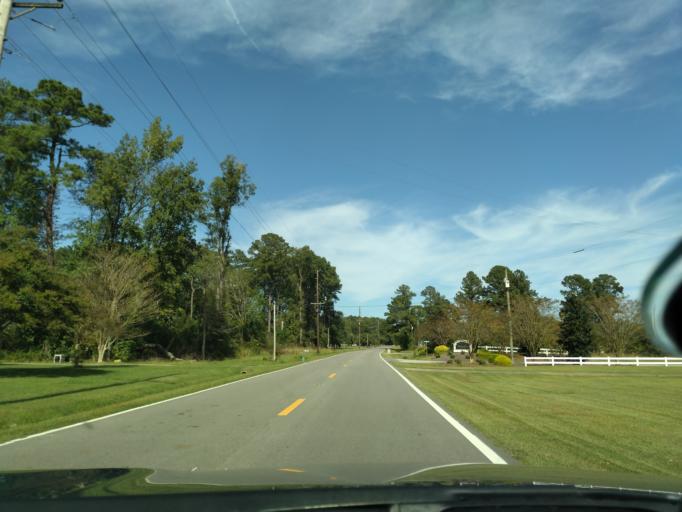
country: US
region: North Carolina
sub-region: Beaufort County
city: River Road
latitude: 35.5233
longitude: -76.9554
